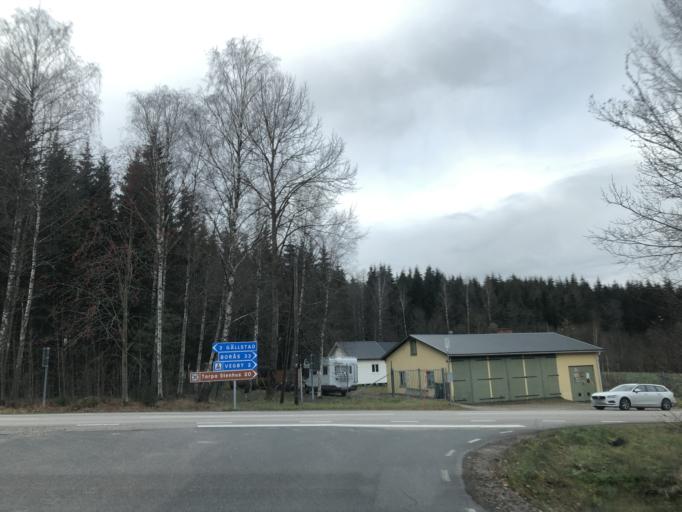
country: SE
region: Vaestra Goetaland
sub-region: Ulricehamns Kommun
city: Ulricehamn
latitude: 57.6747
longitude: 13.4020
